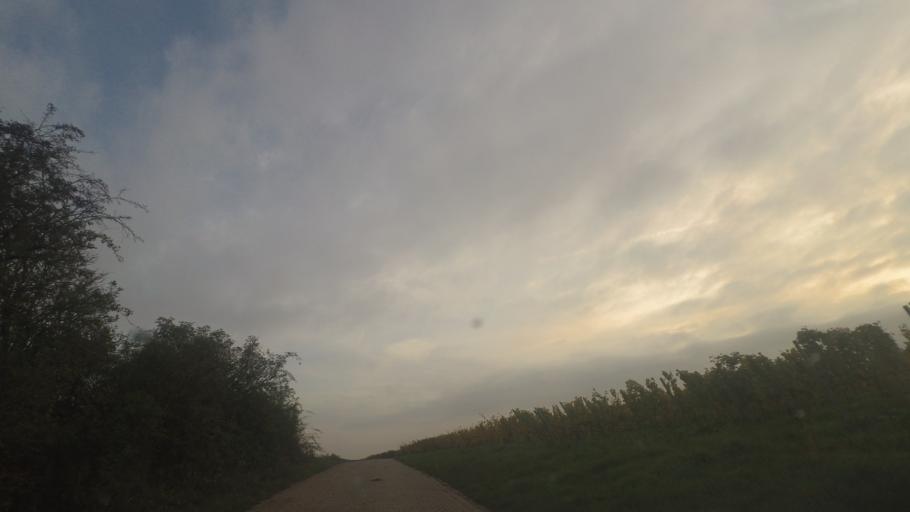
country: DE
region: Rheinland-Pfalz
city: Offstein
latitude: 49.5998
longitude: 8.2630
